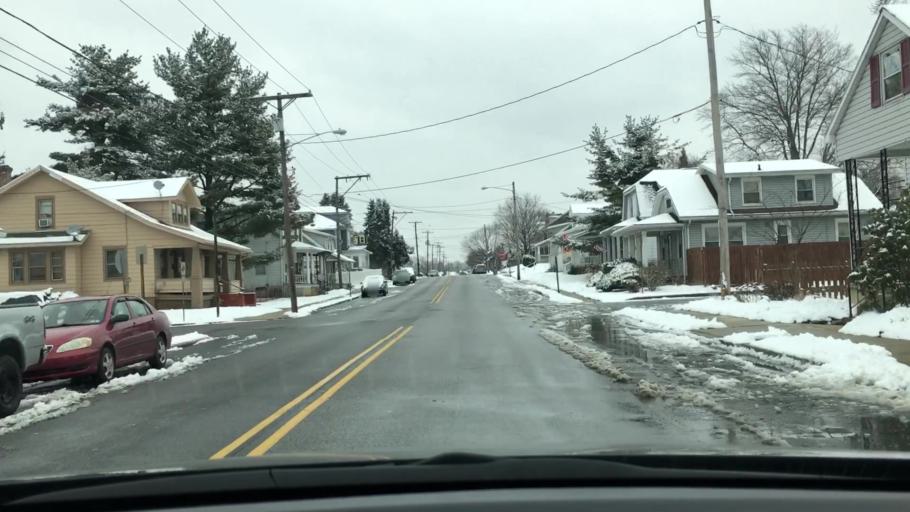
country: US
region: Pennsylvania
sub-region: York County
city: Valley View
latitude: 39.9583
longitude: -76.7091
